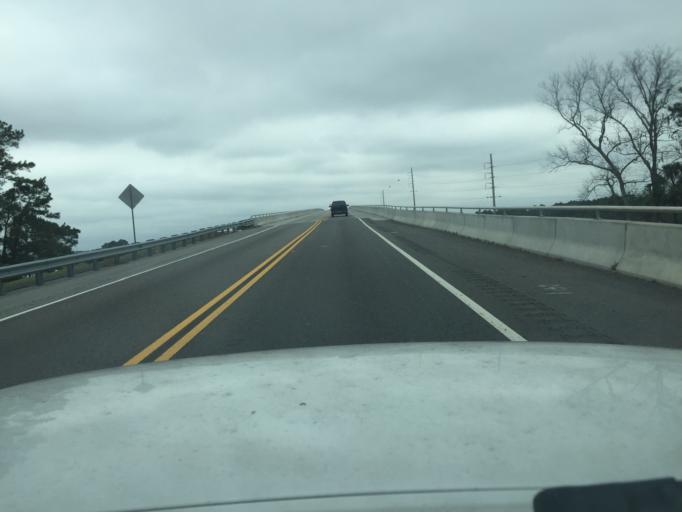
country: US
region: Georgia
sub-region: Chatham County
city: Skidaway Island
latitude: 31.9450
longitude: -81.0625
